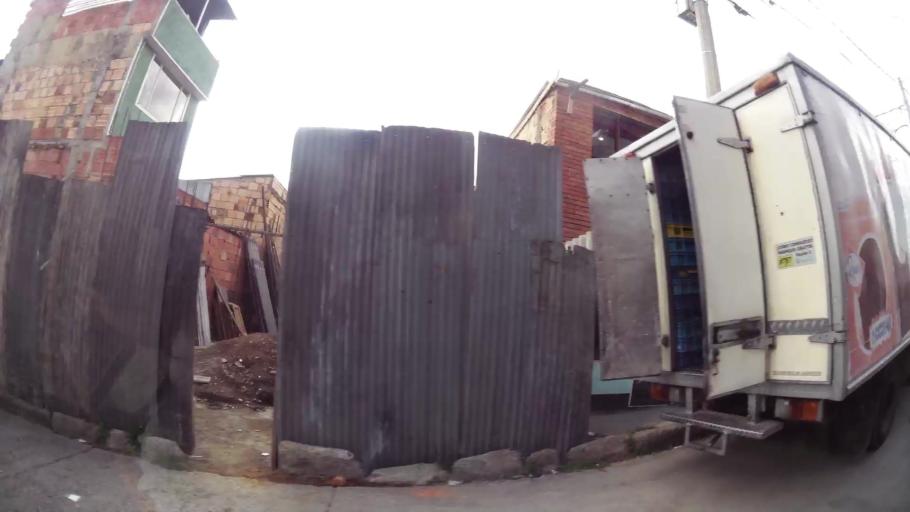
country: CO
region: Cundinamarca
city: Cota
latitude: 4.7256
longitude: -74.0860
